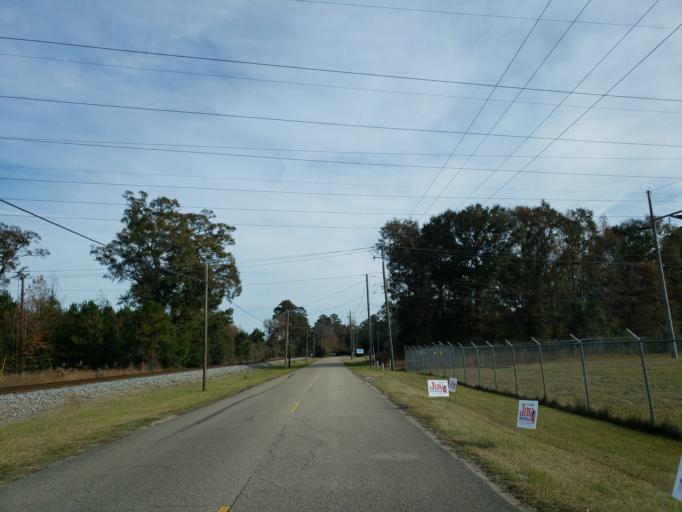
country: US
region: Mississippi
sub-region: Forrest County
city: Glendale
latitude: 31.3509
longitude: -89.3229
